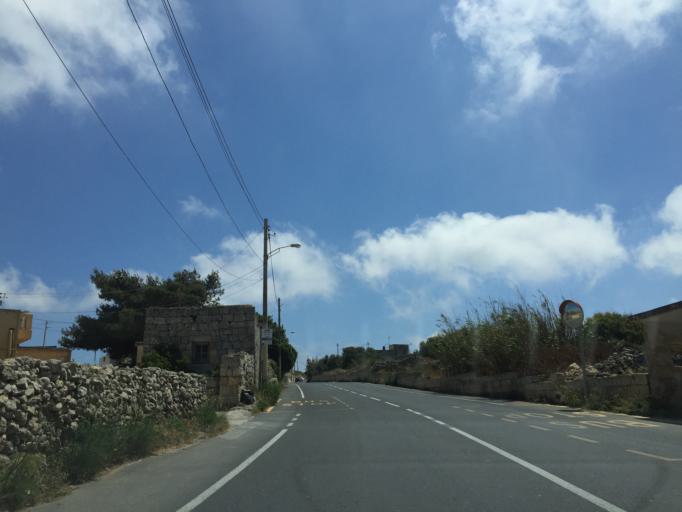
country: MT
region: Dingli
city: Dingli
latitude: 35.8664
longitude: 14.3899
